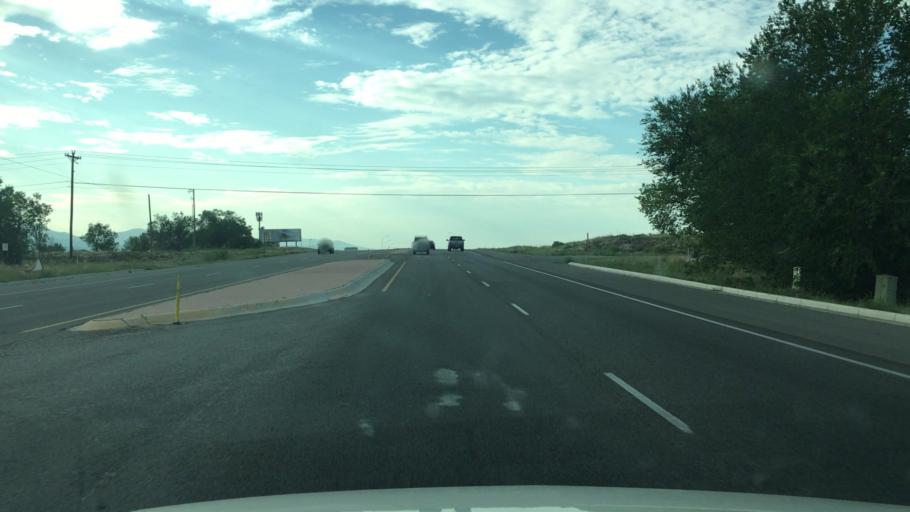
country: US
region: New Mexico
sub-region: Santa Fe County
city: El Valle de Arroyo Seco
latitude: 35.9810
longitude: -106.0483
